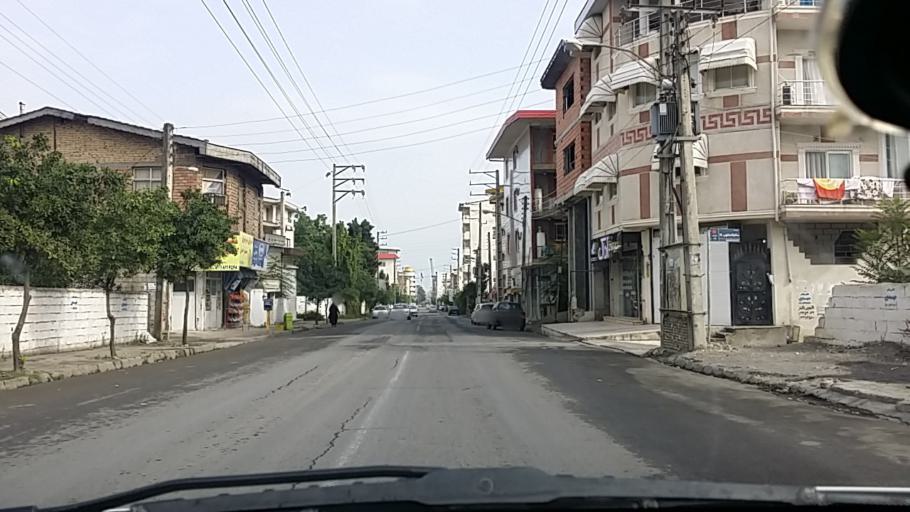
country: IR
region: Mazandaran
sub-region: Nowshahr
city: Nowshahr
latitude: 36.6438
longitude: 51.5084
